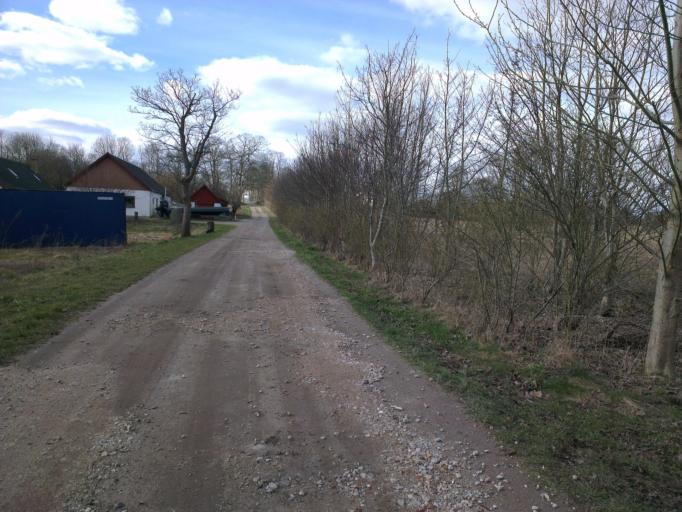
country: DK
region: Capital Region
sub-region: Frederikssund Kommune
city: Frederikssund
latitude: 55.7789
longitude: 12.0444
